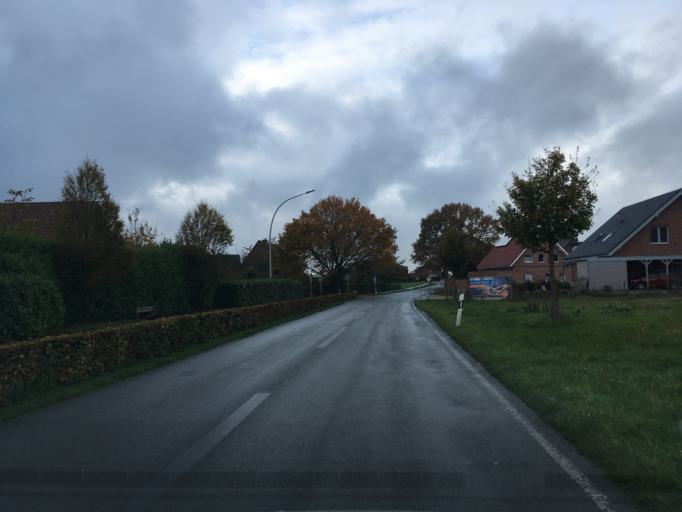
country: DE
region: North Rhine-Westphalia
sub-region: Regierungsbezirk Munster
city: Klein Reken
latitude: 51.8322
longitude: 7.0362
